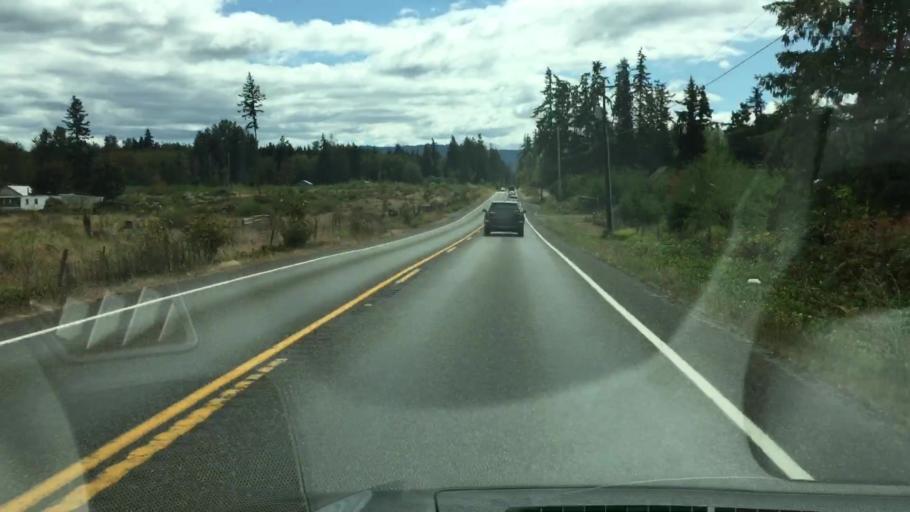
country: US
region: Washington
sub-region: Pierce County
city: Eatonville
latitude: 46.9048
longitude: -122.2979
